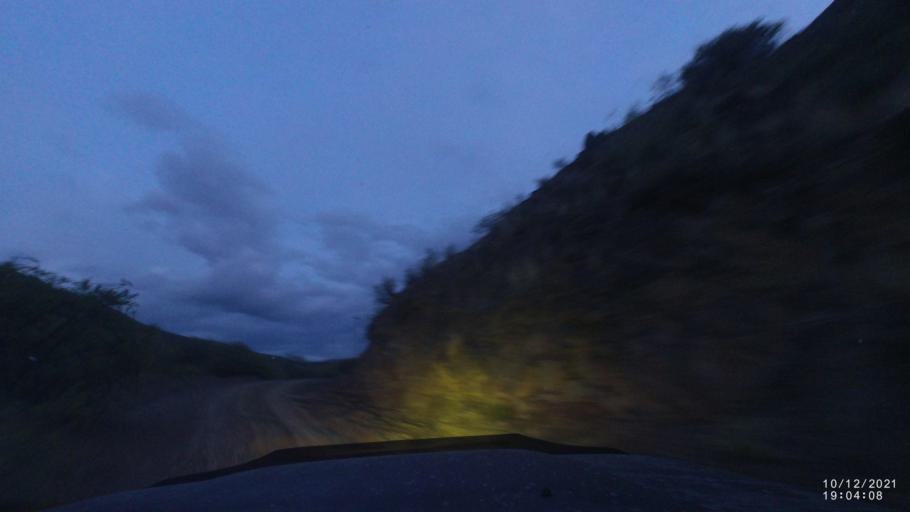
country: BO
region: Cochabamba
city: Tarata
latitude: -17.9018
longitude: -65.9430
